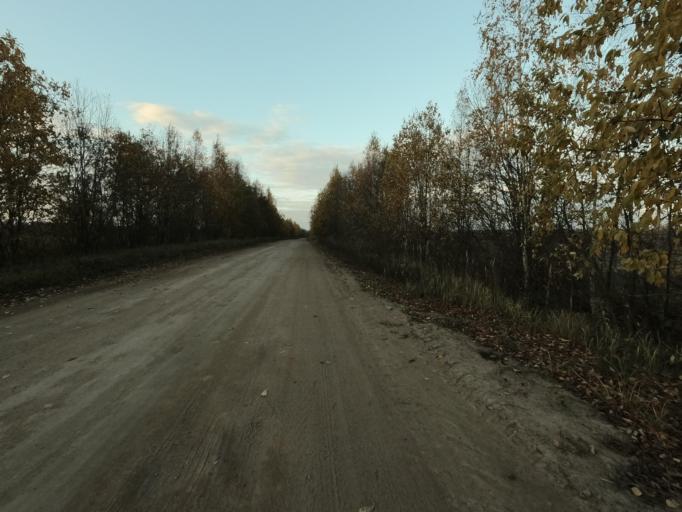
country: RU
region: Leningrad
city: Mga
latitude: 59.8006
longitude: 31.2004
